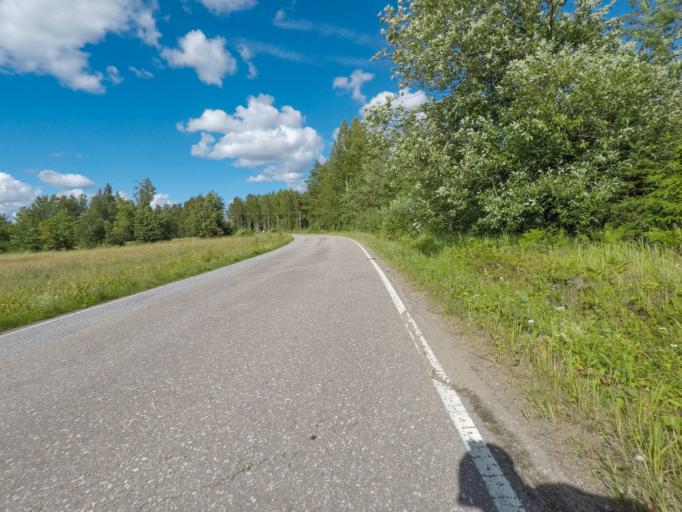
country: FI
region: South Karelia
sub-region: Lappeenranta
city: Joutseno
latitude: 61.1026
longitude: 28.3702
